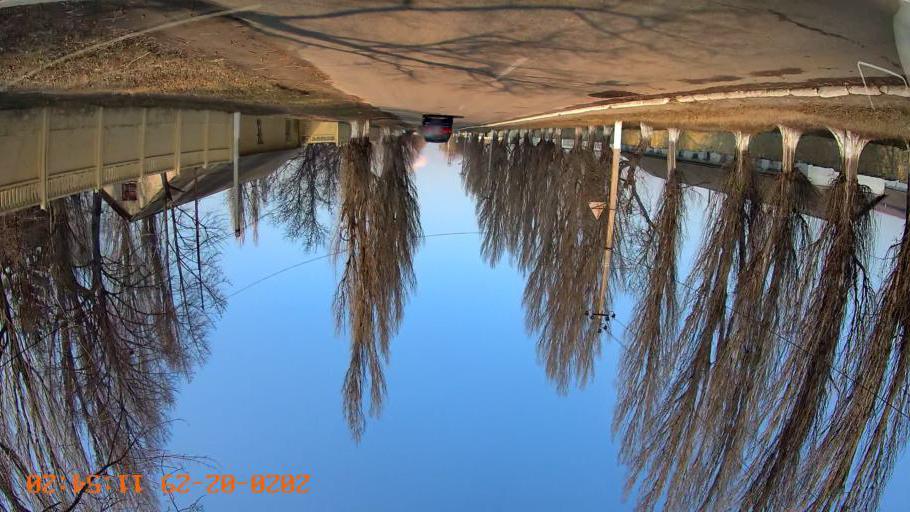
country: MD
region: Telenesti
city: Ribnita
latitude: 47.7838
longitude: 28.9948
